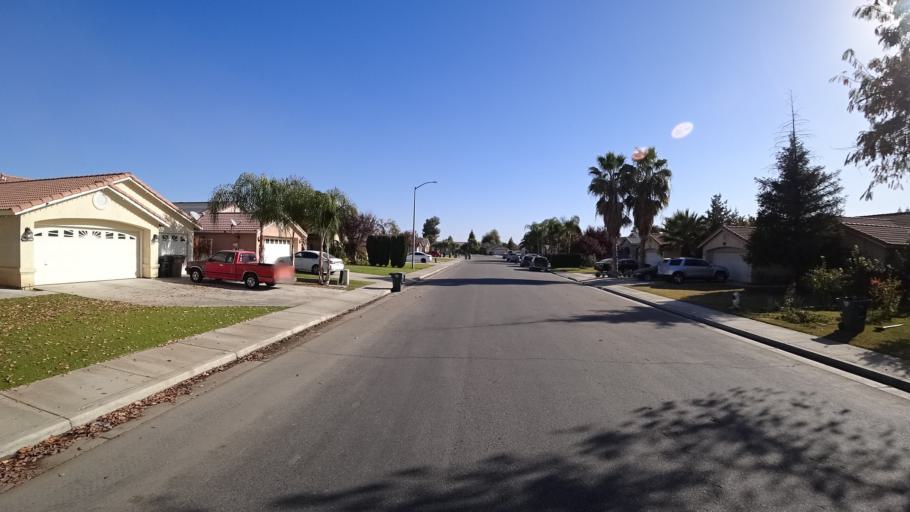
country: US
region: California
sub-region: Kern County
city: Greenfield
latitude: 35.2785
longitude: -119.0346
